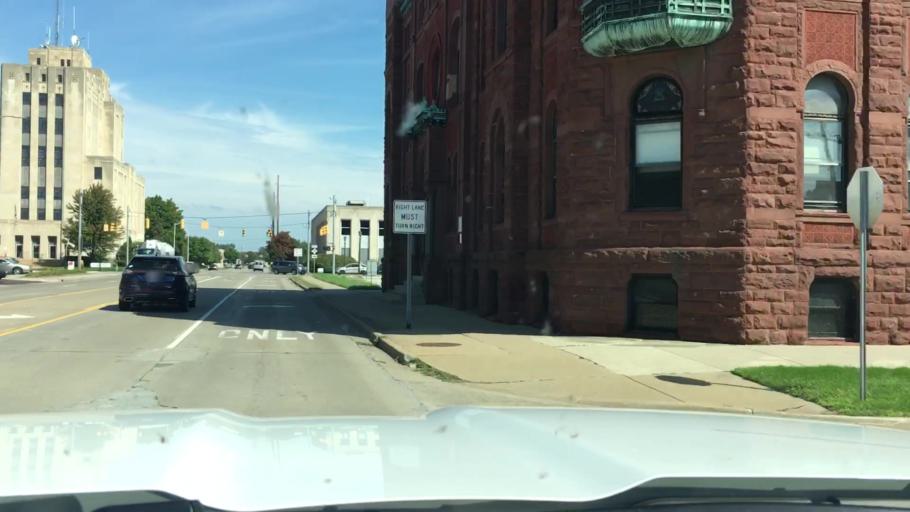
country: US
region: Michigan
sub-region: Bay County
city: Bay City
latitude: 43.5967
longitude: -83.8847
